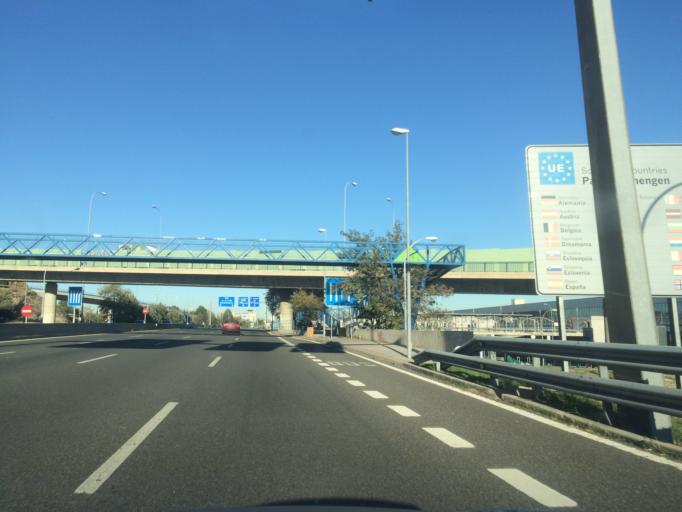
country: ES
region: Madrid
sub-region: Provincia de Madrid
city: Barajas de Madrid
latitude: 40.4603
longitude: -3.5781
